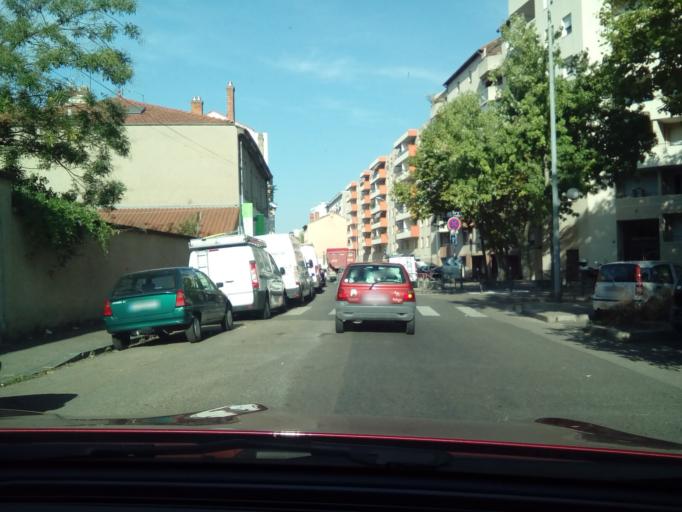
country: FR
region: Rhone-Alpes
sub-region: Departement du Rhone
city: Villeurbanne
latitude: 45.7539
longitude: 4.8943
